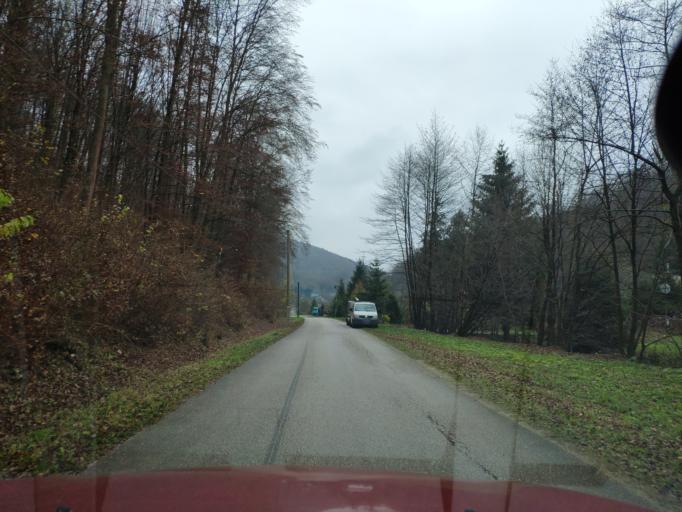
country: SK
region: Kosicky
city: Roznava
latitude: 48.7006
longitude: 20.5467
